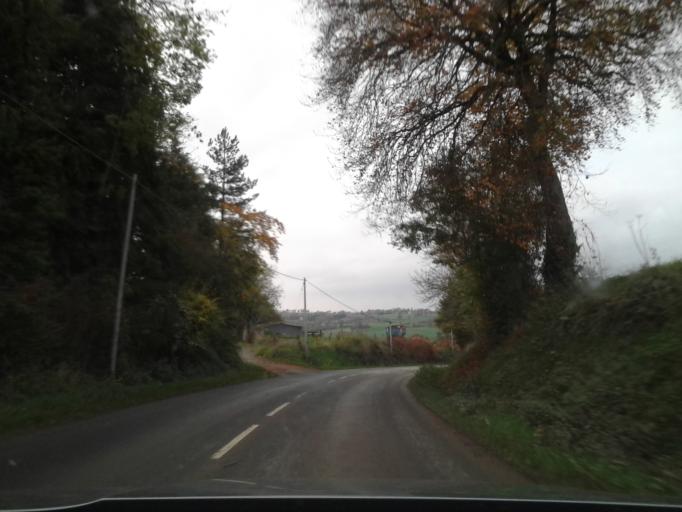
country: FR
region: Lower Normandy
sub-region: Departement du Calvados
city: Le Theil-Bocage
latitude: 48.8823
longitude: -0.7197
